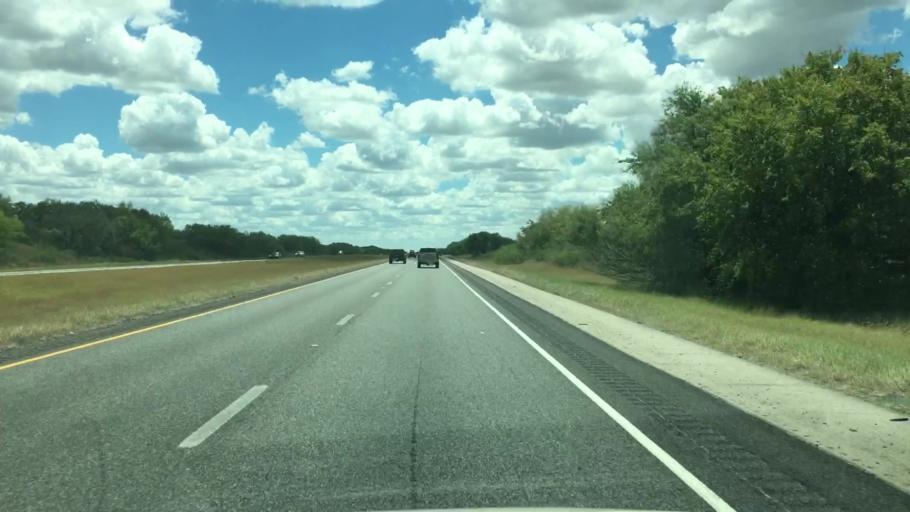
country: US
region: Texas
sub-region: Atascosa County
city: Pleasanton
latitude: 29.0827
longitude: -98.4331
